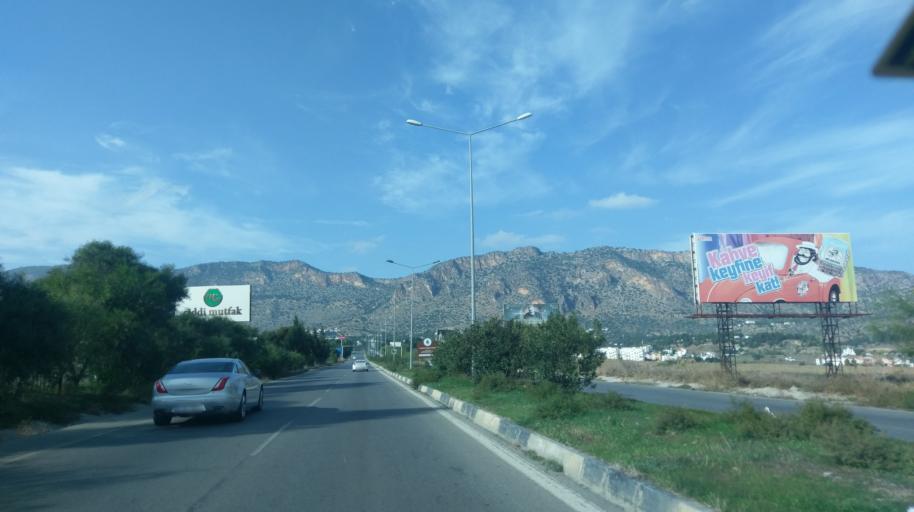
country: CY
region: Keryneia
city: Kyrenia
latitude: 35.2784
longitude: 33.2843
